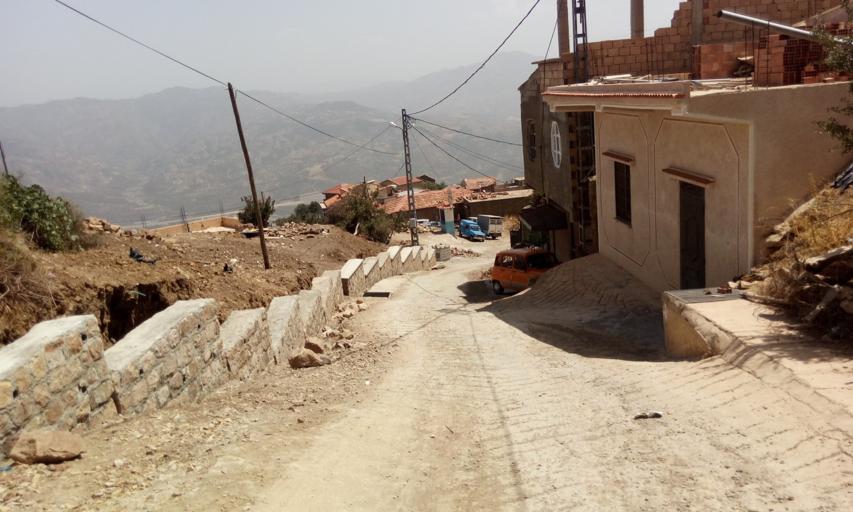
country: DZ
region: Tizi Ouzou
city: Chemini
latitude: 36.6090
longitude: 4.6325
